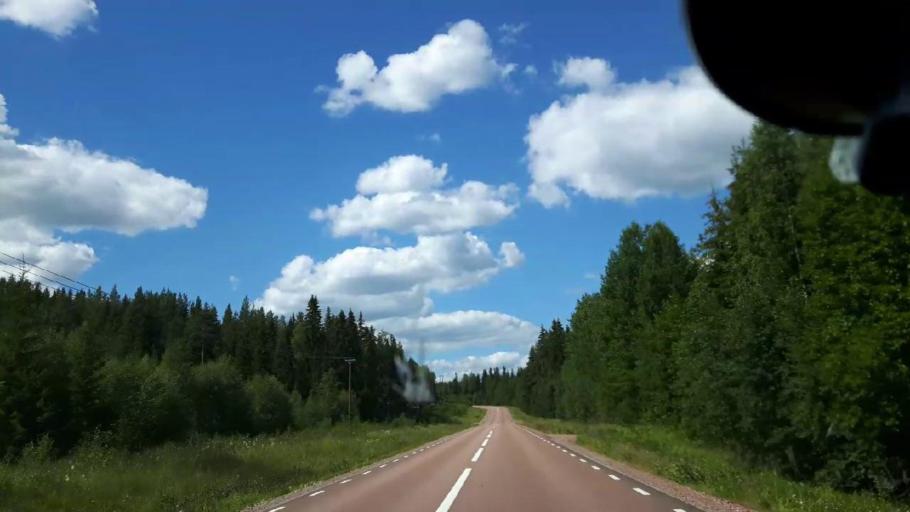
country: SE
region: Jaemtland
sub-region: Ragunda Kommun
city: Hammarstrand
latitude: 63.0163
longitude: 16.6170
